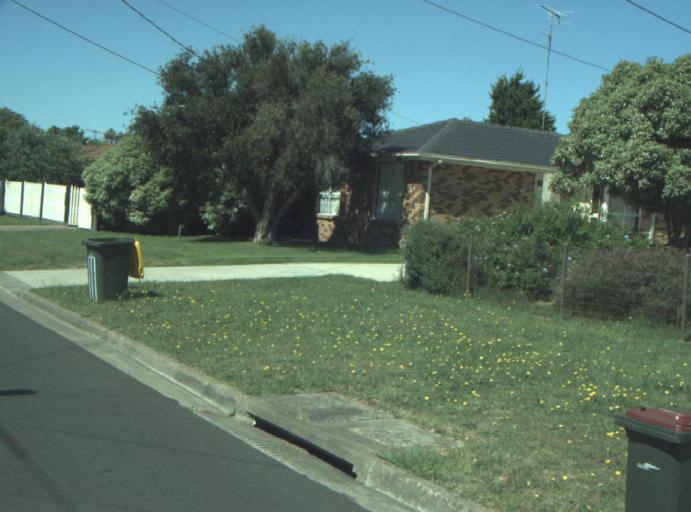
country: AU
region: Victoria
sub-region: Greater Geelong
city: Breakwater
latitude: -38.1879
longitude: 144.3466
